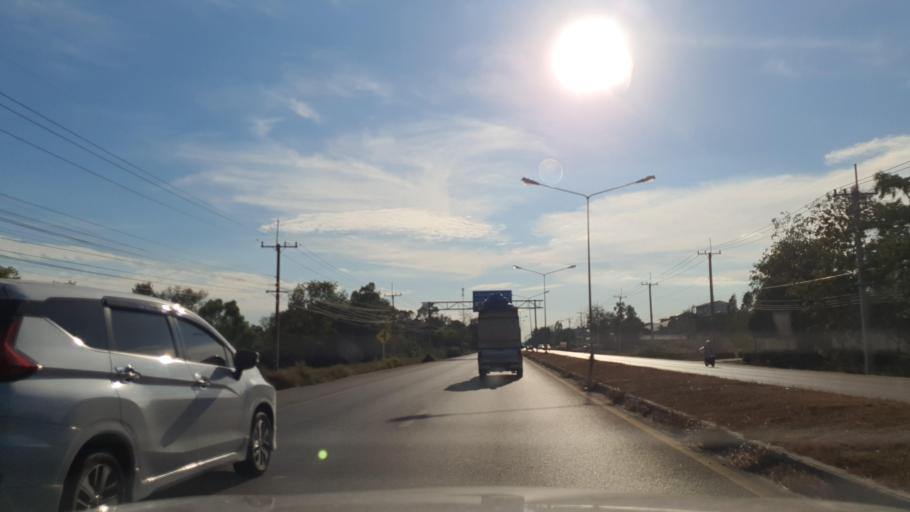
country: TH
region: Kalasin
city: Yang Talat
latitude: 16.3603
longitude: 103.3380
